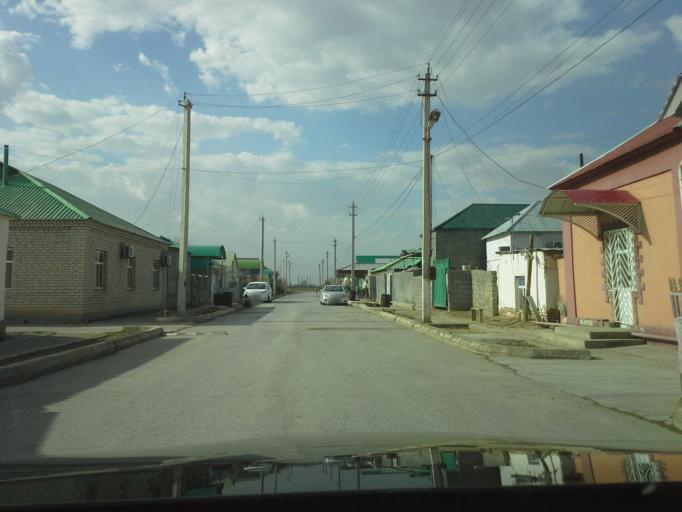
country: TM
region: Ahal
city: Ashgabat
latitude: 37.9925
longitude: 58.2944
